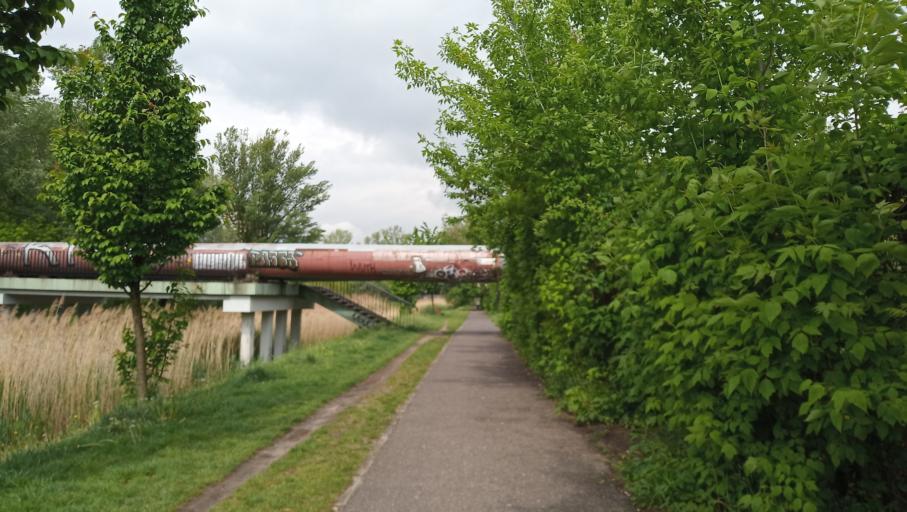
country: PL
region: Masovian Voivodeship
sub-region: Warszawa
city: Zoliborz
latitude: 52.2810
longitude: 20.9878
